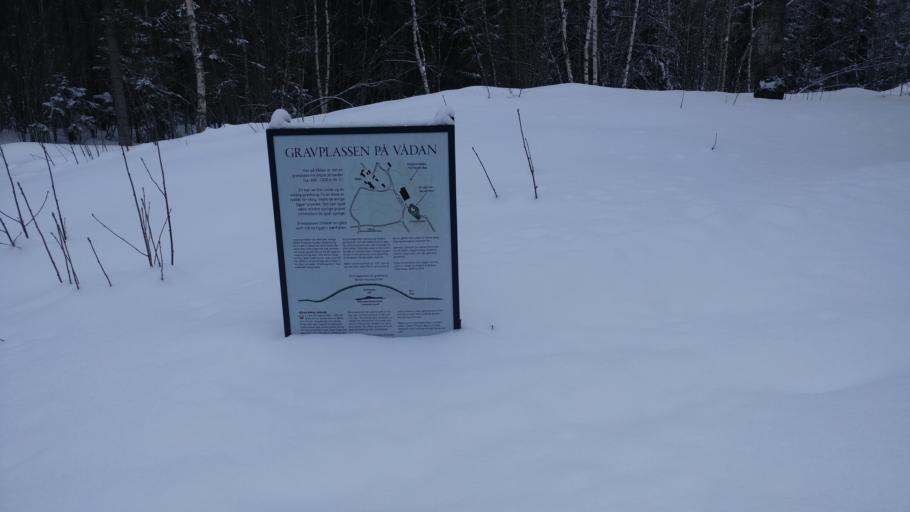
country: NO
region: Sor-Trondelag
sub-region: Trondheim
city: Trondheim
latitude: 63.3903
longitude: 10.3038
